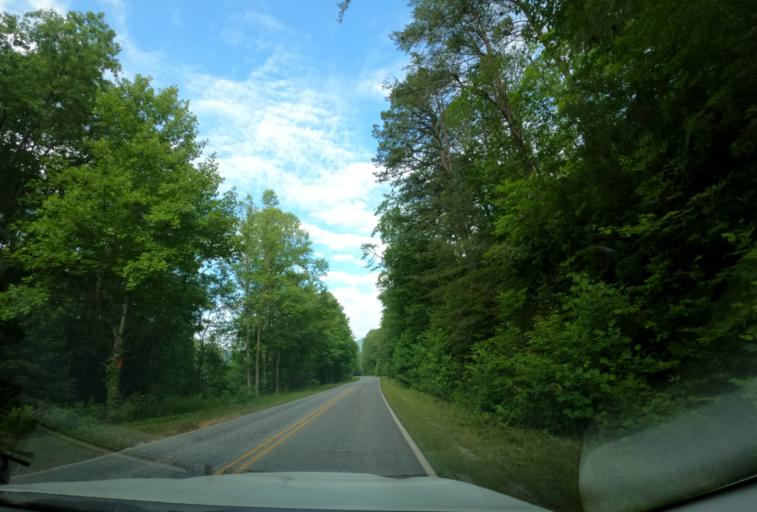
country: US
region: North Carolina
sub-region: Transylvania County
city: Brevard
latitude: 35.1892
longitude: -82.9056
